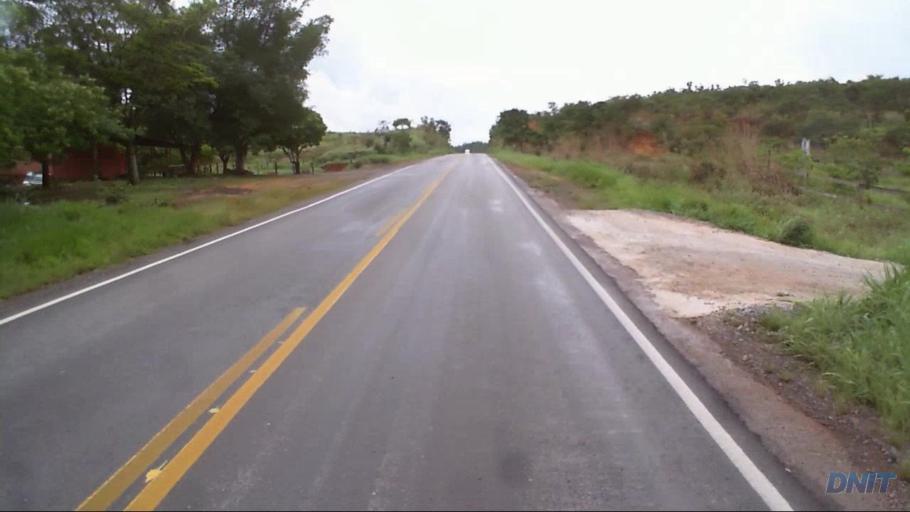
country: BR
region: Goias
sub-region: Padre Bernardo
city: Padre Bernardo
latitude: -15.4859
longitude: -48.2332
